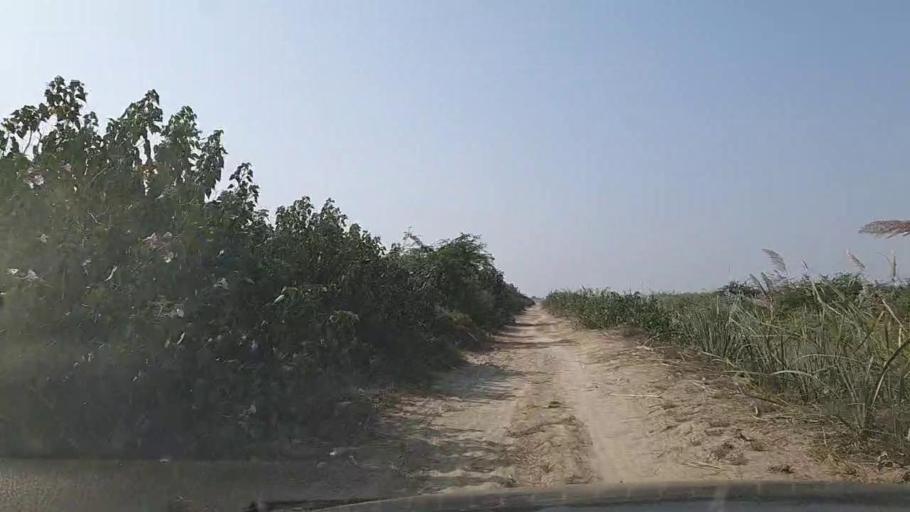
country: PK
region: Sindh
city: Gharo
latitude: 24.7182
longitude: 67.6622
